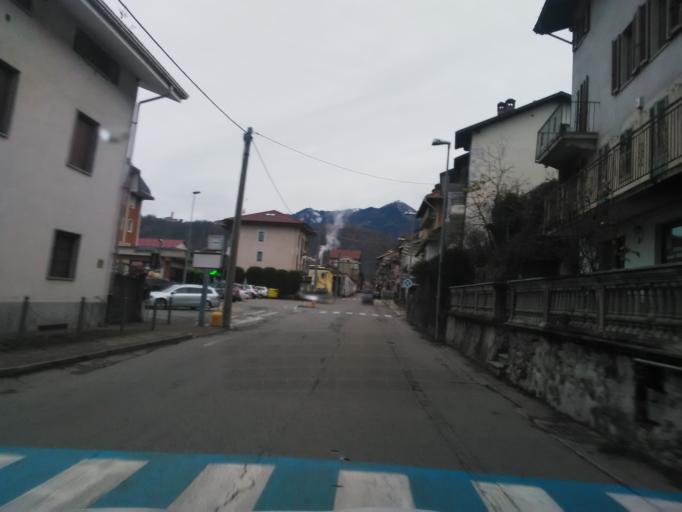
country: IT
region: Piedmont
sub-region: Provincia di Biella
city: Pray
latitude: 45.6754
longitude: 8.2114
